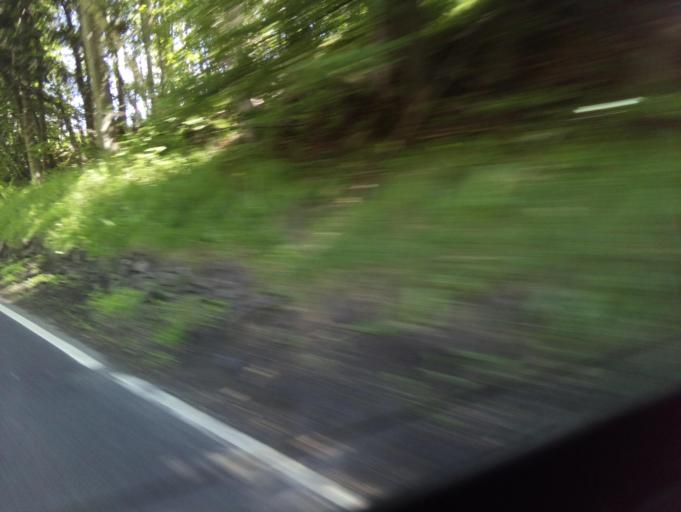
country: GB
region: Scotland
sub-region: The Scottish Borders
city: Galashiels
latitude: 55.6767
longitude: -2.8658
